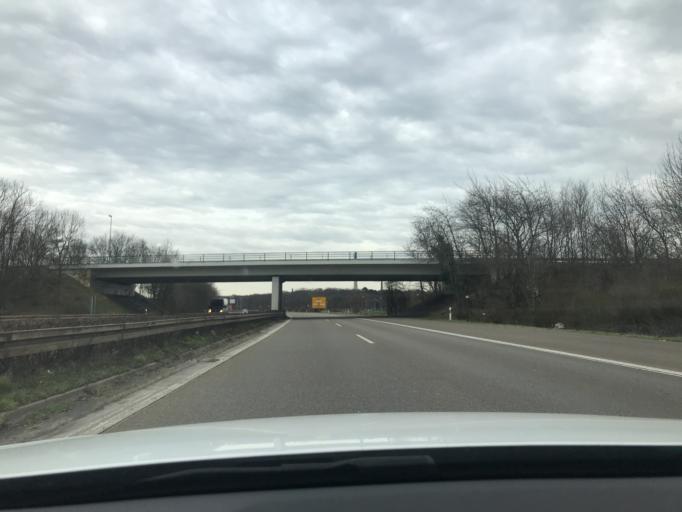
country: DE
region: North Rhine-Westphalia
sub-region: Regierungsbezirk Dusseldorf
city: Krefeld
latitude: 51.3720
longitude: 6.6347
